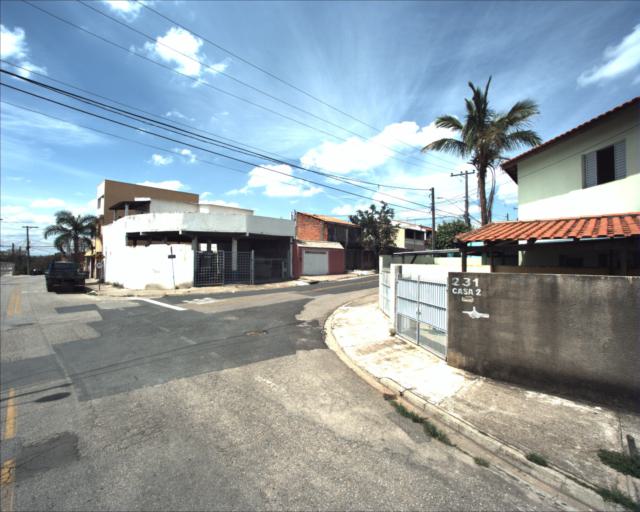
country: BR
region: Sao Paulo
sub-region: Sorocaba
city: Sorocaba
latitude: -23.4116
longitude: -47.4106
